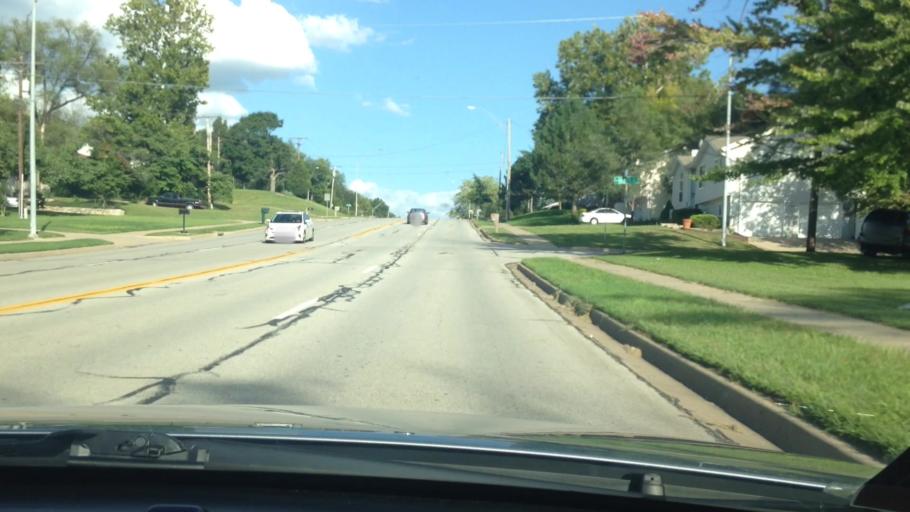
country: US
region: Missouri
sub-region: Clay County
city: Claycomo
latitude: 39.1806
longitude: -94.5162
